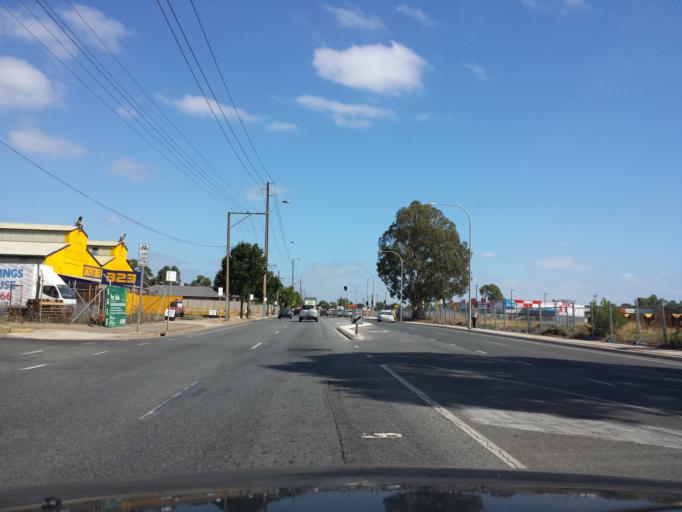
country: AU
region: South Australia
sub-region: Prospect
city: Prospect
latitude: -34.8698
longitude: 138.5838
